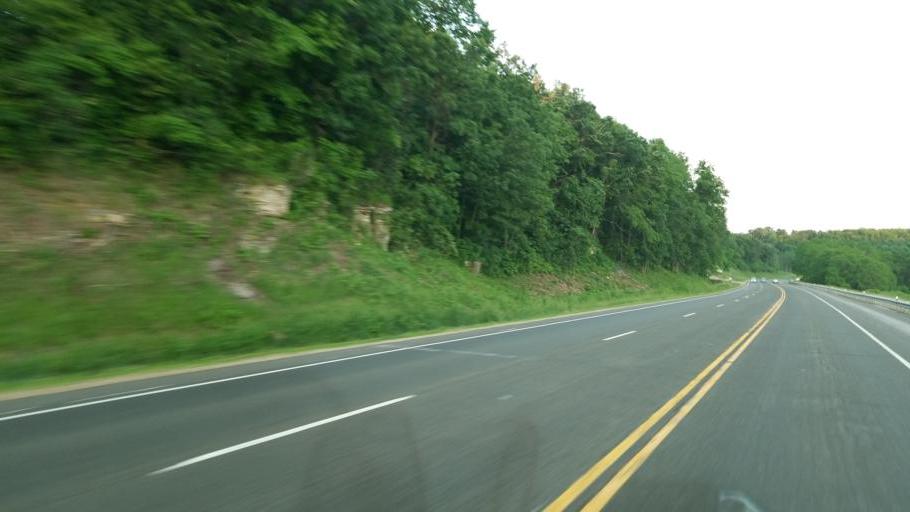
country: US
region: Wisconsin
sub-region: Monroe County
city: Tomah
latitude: 43.8917
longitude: -90.4854
